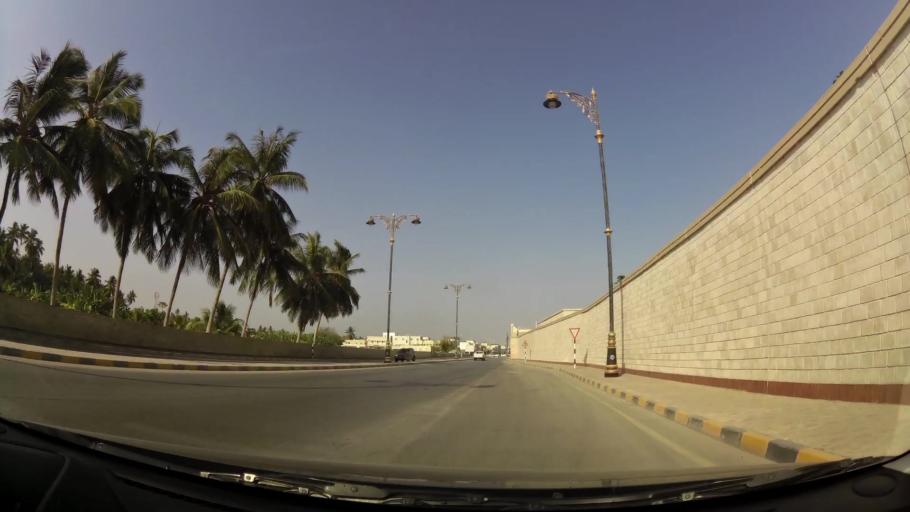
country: OM
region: Zufar
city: Salalah
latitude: 17.0019
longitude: 54.0999
